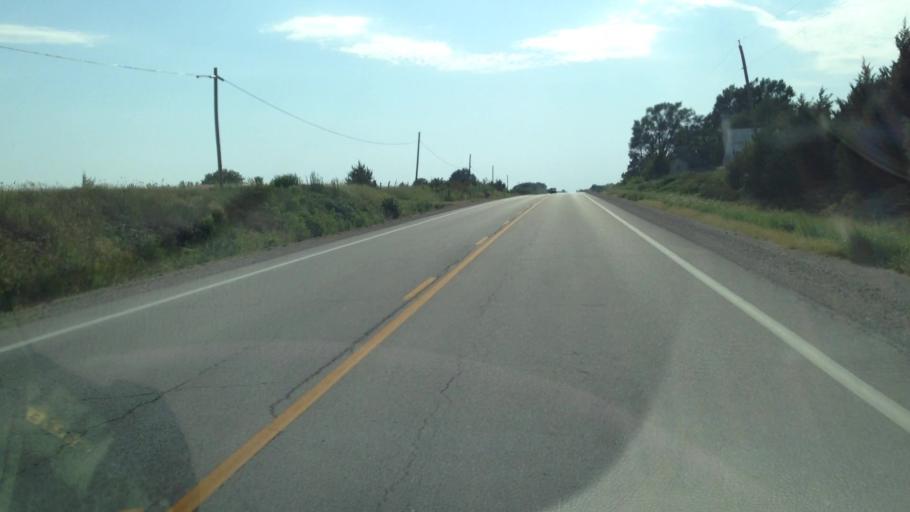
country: US
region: Kansas
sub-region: Anderson County
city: Garnett
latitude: 38.0816
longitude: -95.1818
